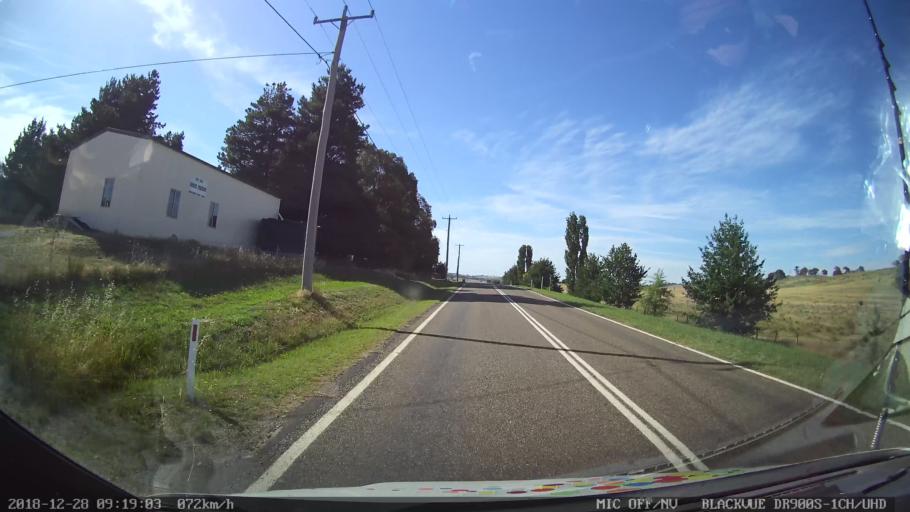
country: AU
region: New South Wales
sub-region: Upper Lachlan Shire
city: Crookwell
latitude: -34.3323
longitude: 149.3668
